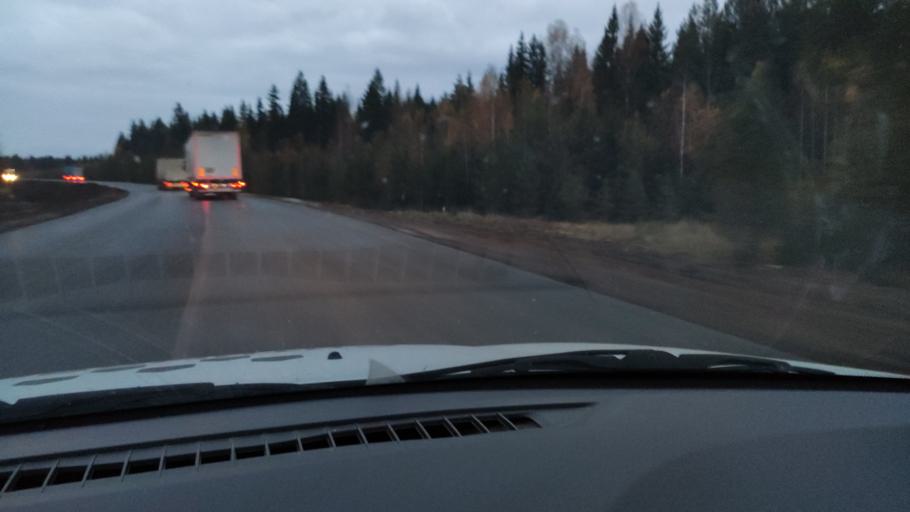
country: RU
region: Kirov
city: Kostino
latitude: 58.8193
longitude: 53.3155
